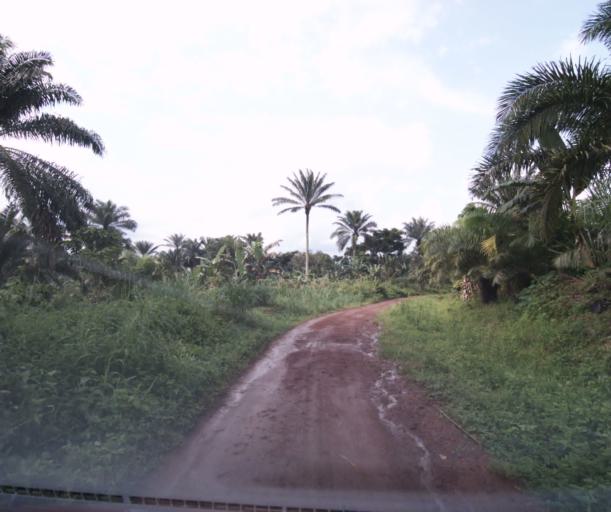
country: CM
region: Littoral
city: Melong
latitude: 5.0591
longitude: 9.9697
